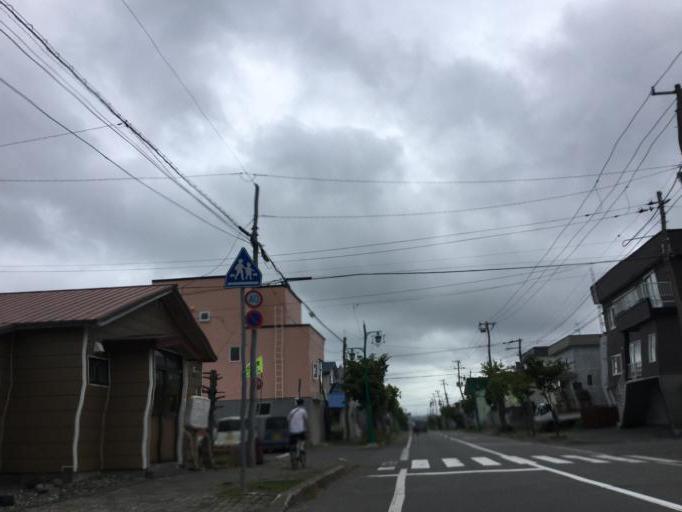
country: JP
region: Hokkaido
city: Wakkanai
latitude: 45.3894
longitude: 141.6997
